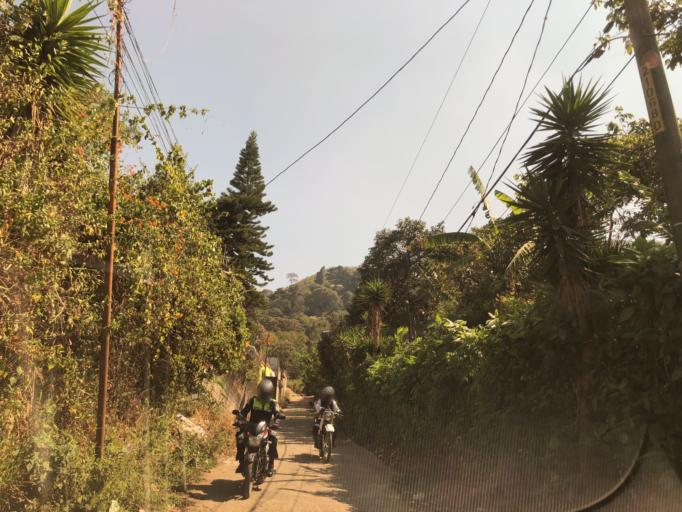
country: GT
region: Guatemala
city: Santa Catarina Pinula
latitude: 14.5391
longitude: -90.5048
